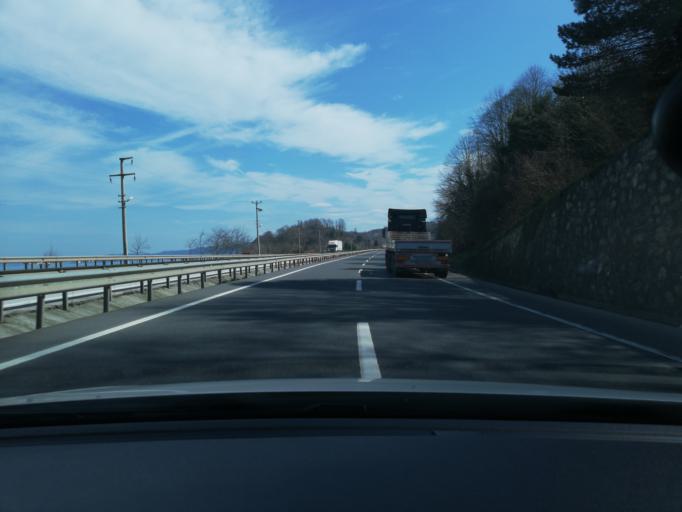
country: TR
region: Duzce
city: Akcakoca
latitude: 41.0967
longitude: 31.2095
